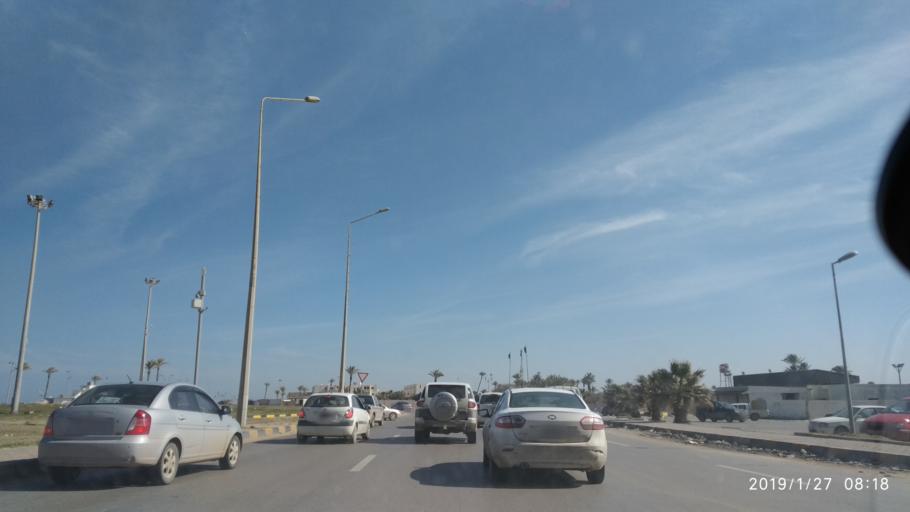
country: LY
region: Tripoli
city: Tripoli
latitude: 32.9067
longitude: 13.2666
